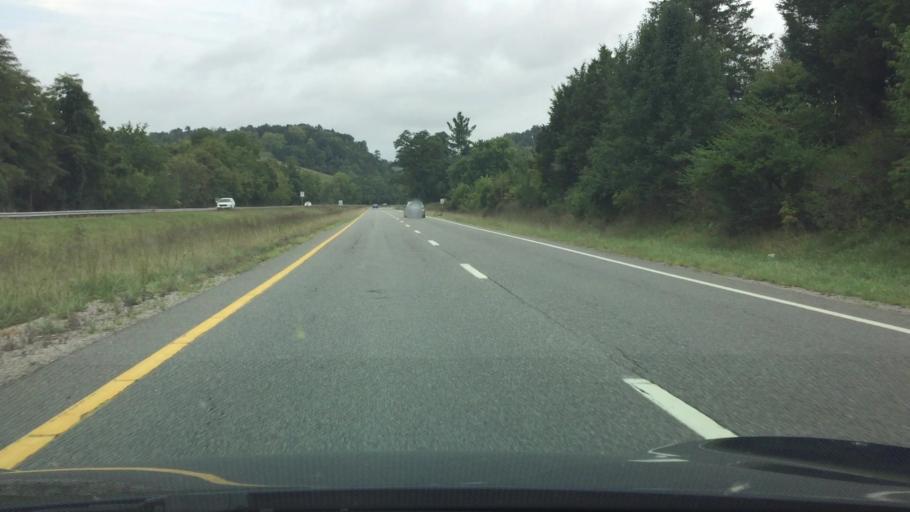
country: US
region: Virginia
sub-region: City of Radford
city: Radford
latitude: 37.1029
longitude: -80.5176
